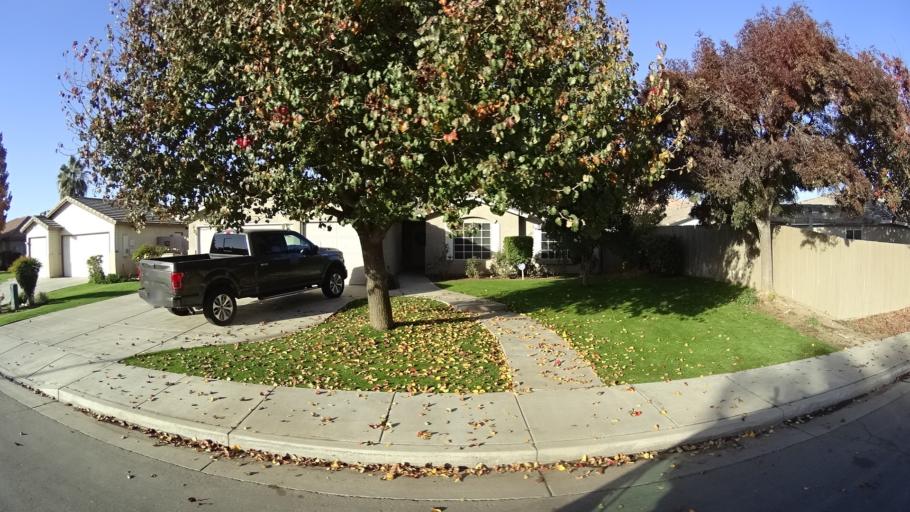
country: US
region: California
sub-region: Kern County
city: Greenfield
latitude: 35.2774
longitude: -119.0280
